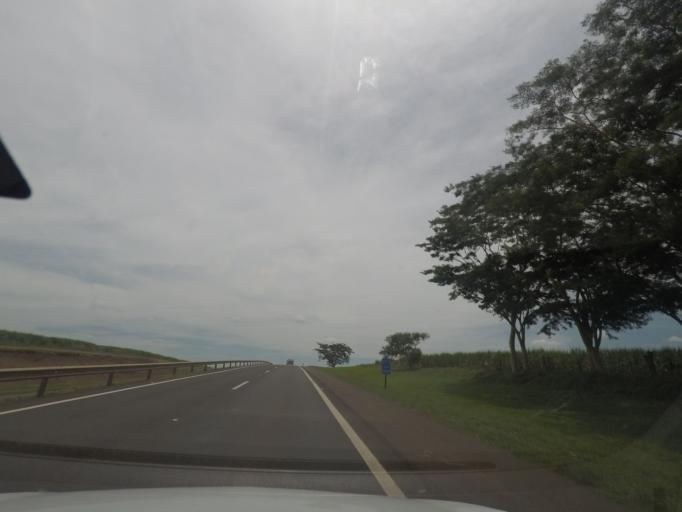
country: BR
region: Sao Paulo
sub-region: Bebedouro
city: Bebedouro
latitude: -21.0467
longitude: -48.4156
